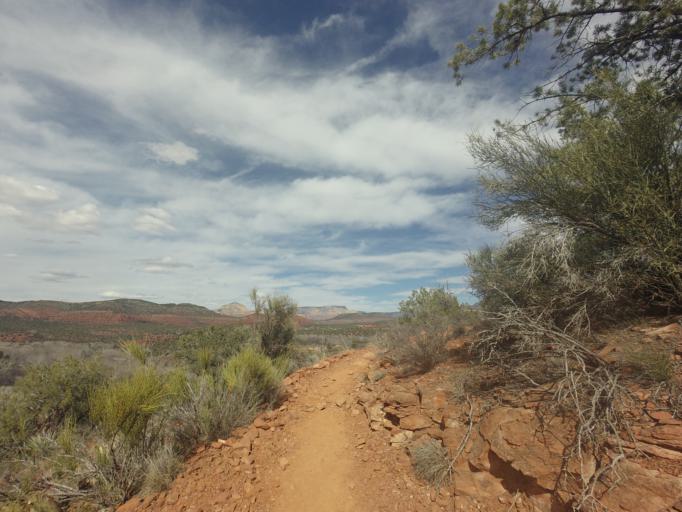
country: US
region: Arizona
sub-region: Yavapai County
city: West Sedona
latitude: 34.8068
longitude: -111.8303
